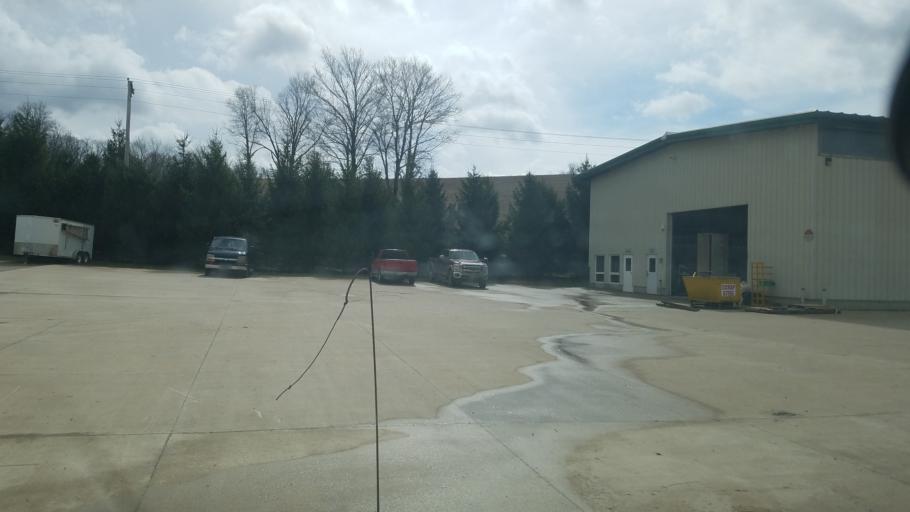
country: US
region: Ohio
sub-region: Knox County
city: Danville
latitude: 40.5515
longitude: -82.3217
